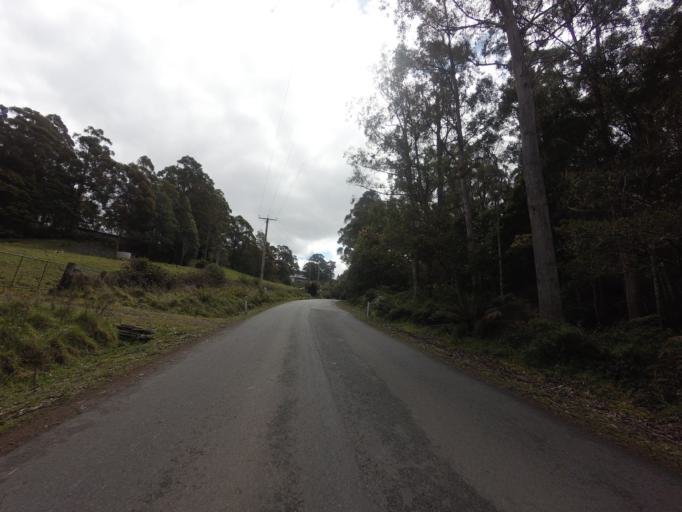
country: AU
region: Tasmania
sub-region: Huon Valley
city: Geeveston
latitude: -43.4179
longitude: 146.9653
